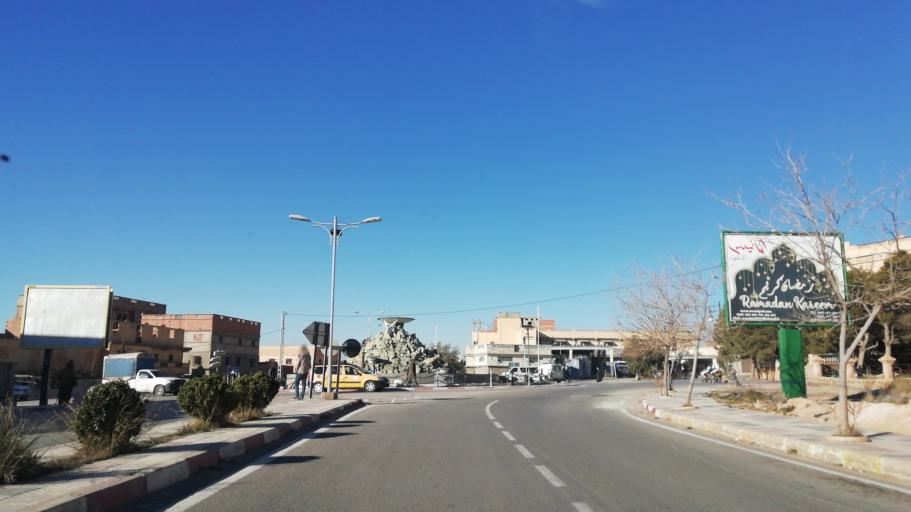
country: DZ
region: El Bayadh
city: El Bayadh
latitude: 33.6855
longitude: 1.0312
